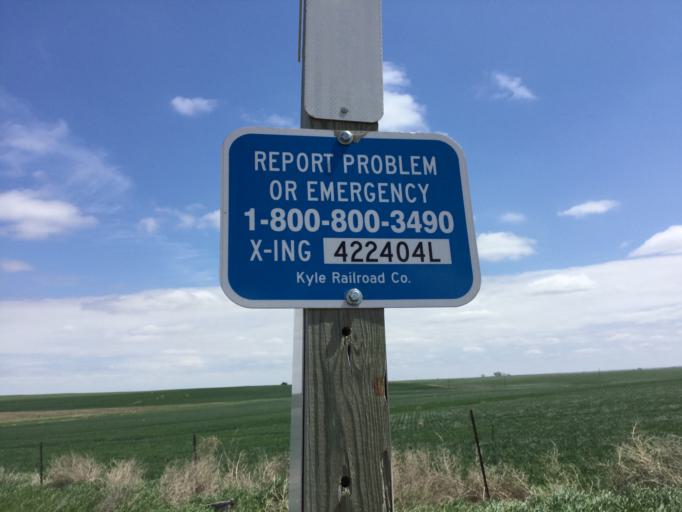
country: US
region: Kansas
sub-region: Osborne County
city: Osborne
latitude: 39.4532
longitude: -98.6008
